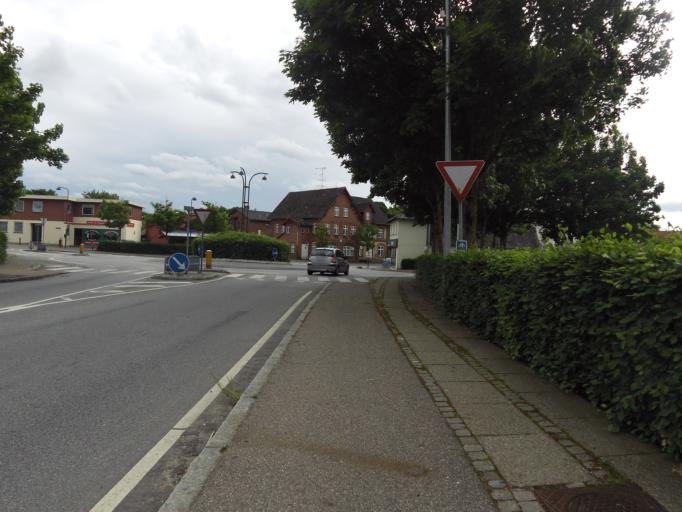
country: DK
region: South Denmark
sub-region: Haderslev Kommune
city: Gram
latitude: 55.2884
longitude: 9.0500
